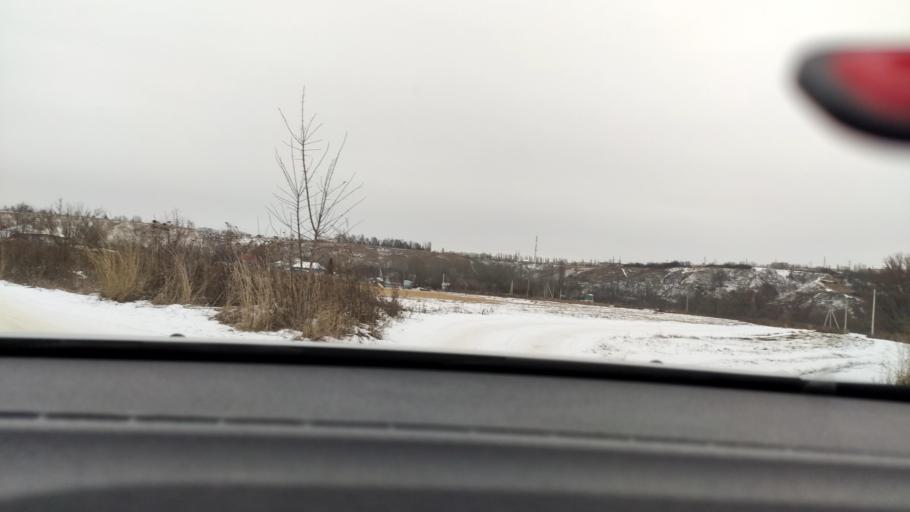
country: RU
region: Voronezj
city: Semiluki
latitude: 51.7004
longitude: 38.9970
